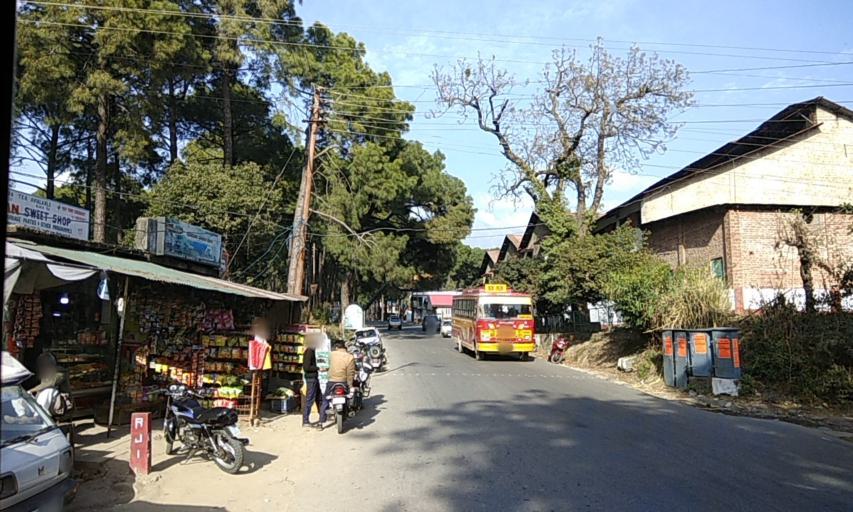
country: IN
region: Himachal Pradesh
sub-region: Kangra
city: Palampur
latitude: 32.0879
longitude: 76.5250
